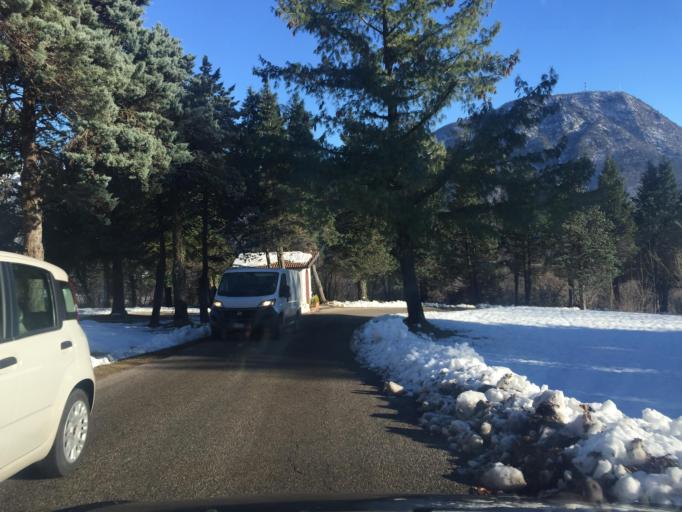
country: IT
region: Friuli Venezia Giulia
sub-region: Provincia di Udine
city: Tolmezzo
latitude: 46.4212
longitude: 12.9998
